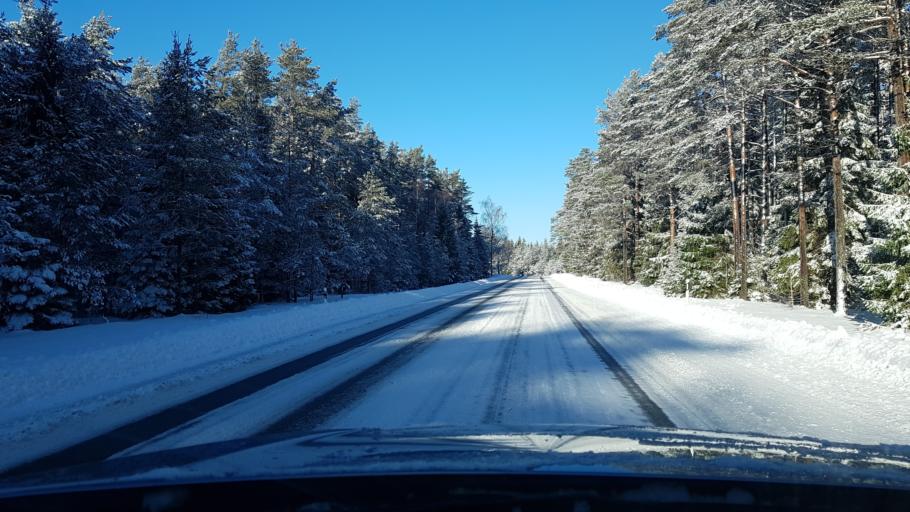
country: EE
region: Hiiumaa
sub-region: Kaerdla linn
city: Kardla
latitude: 58.9336
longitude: 22.7825
